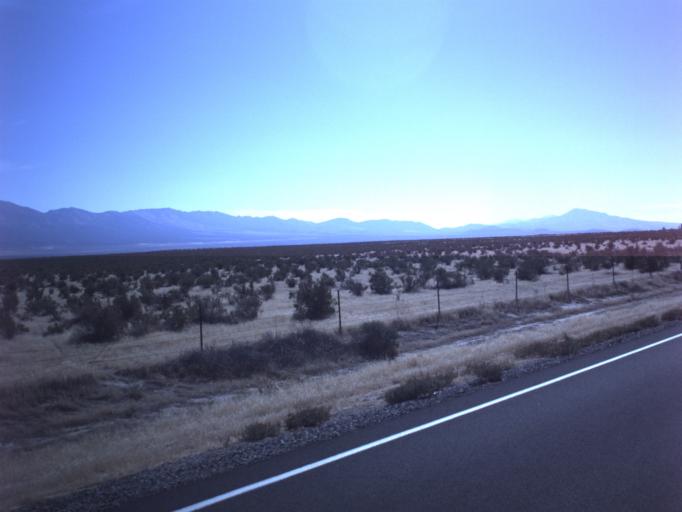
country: US
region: Utah
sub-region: Tooele County
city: Grantsville
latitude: 40.3284
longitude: -112.7442
